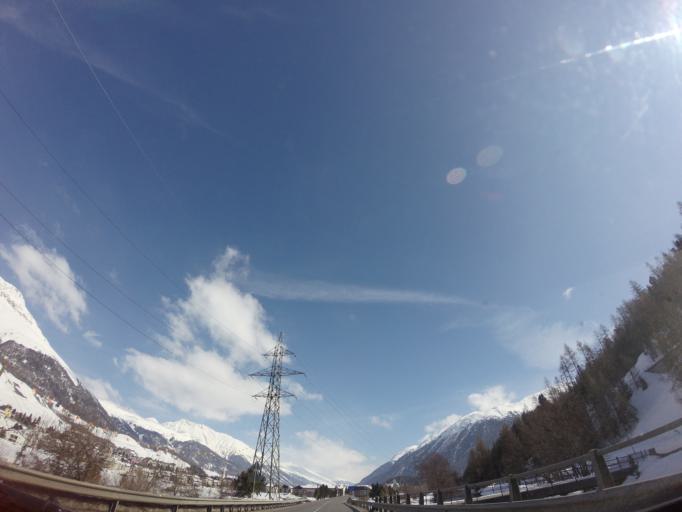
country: CH
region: Grisons
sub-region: Maloja District
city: Celerina
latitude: 46.5059
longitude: 9.8571
